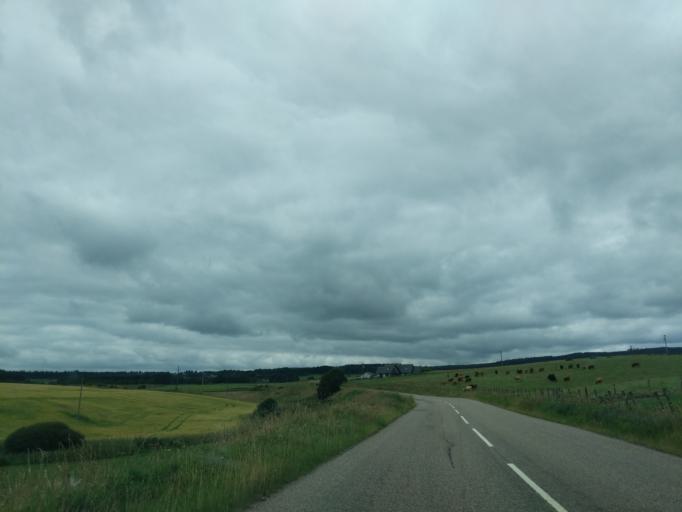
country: GB
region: Scotland
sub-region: Moray
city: Rothes
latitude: 57.4907
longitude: -3.2237
